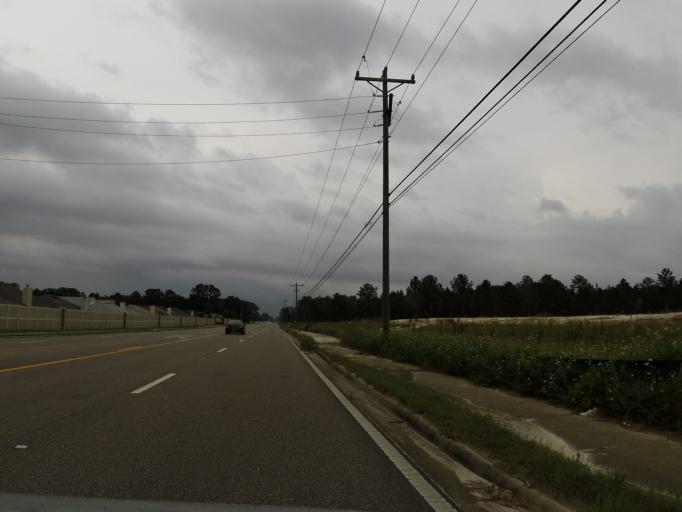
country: US
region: Florida
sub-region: Clay County
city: Middleburg
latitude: 30.1144
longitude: -81.8270
